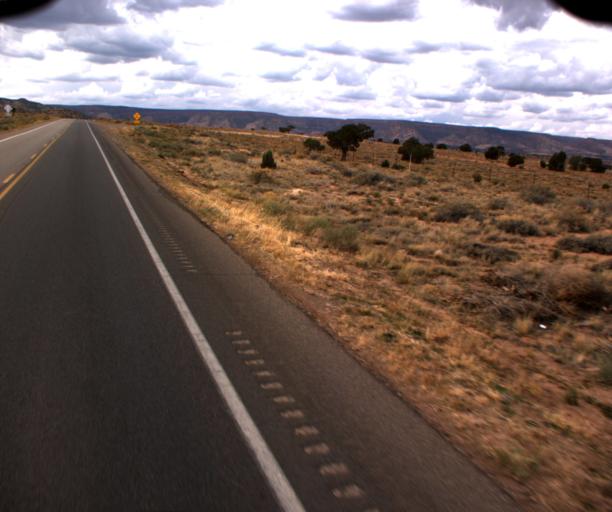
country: US
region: Arizona
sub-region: Navajo County
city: Kayenta
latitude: 36.7007
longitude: -110.2938
